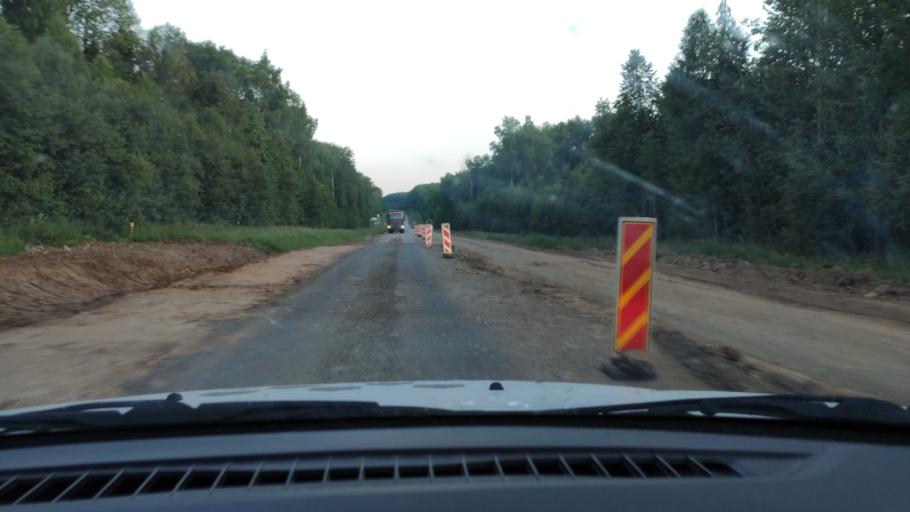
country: RU
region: Perm
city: Siva
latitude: 58.4913
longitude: 54.3559
